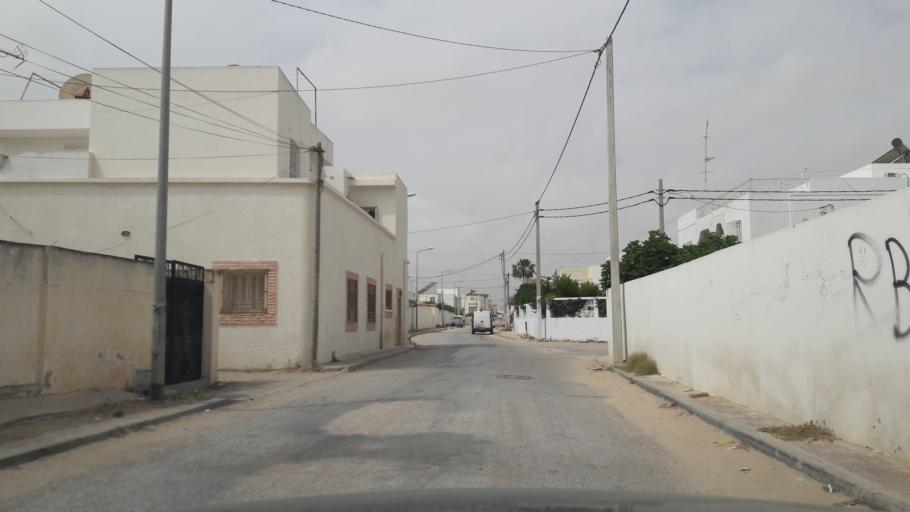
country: TN
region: Safaqis
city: Sfax
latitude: 34.7747
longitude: 10.7585
